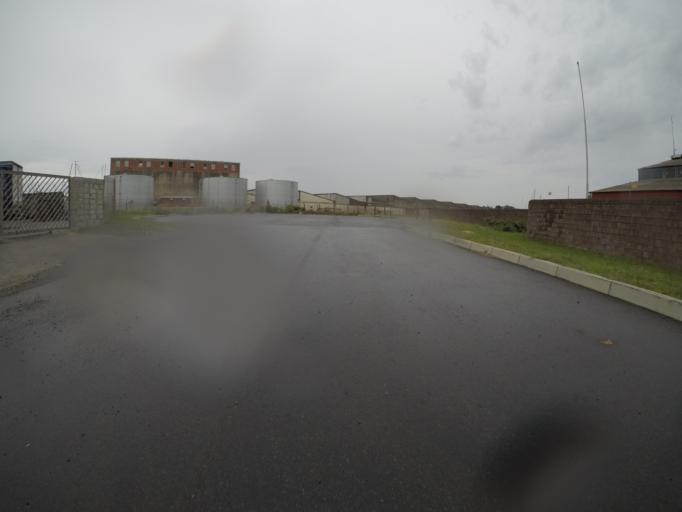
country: ZA
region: Eastern Cape
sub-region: Buffalo City Metropolitan Municipality
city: East London
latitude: -32.9708
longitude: 27.8212
